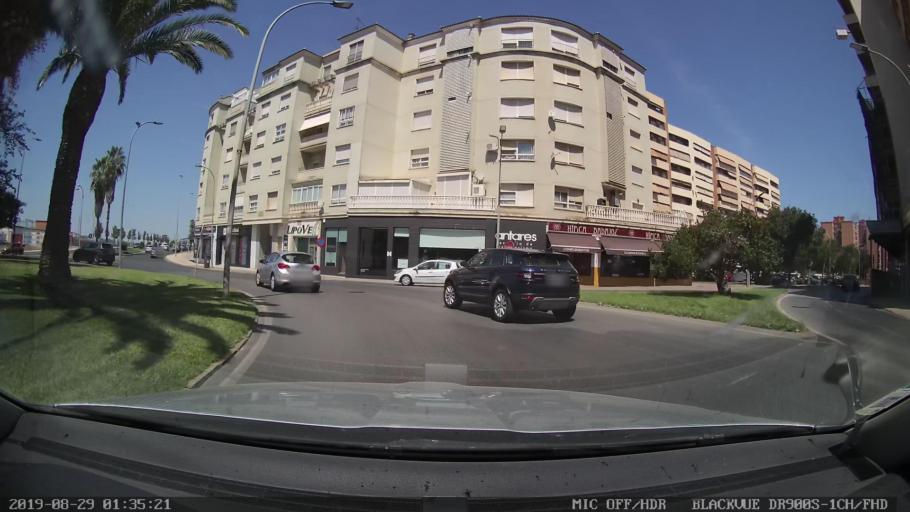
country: ES
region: Extremadura
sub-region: Provincia de Badajoz
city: Badajoz
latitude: 38.8720
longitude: -6.9896
